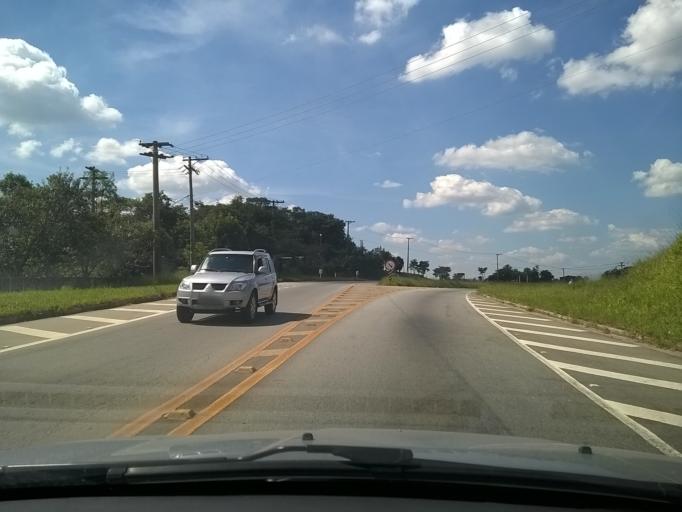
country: BR
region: Sao Paulo
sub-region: Francisco Morato
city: Francisco Morato
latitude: -23.2957
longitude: -46.7661
